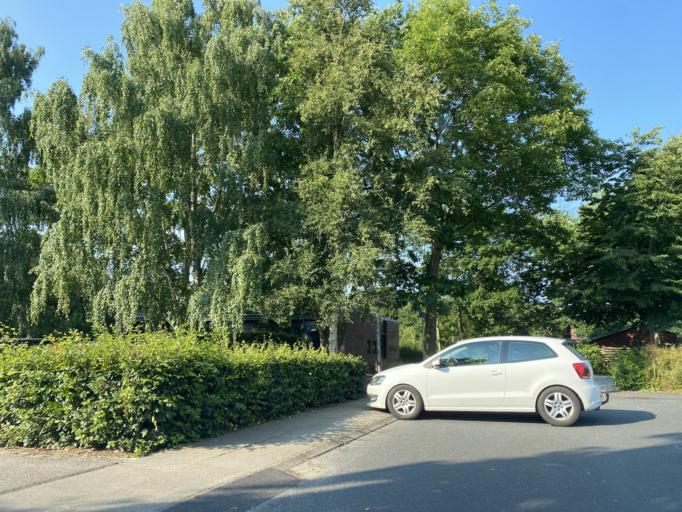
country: DK
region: Central Jutland
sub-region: Viborg Kommune
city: Bjerringbro
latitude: 56.3067
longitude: 9.5872
